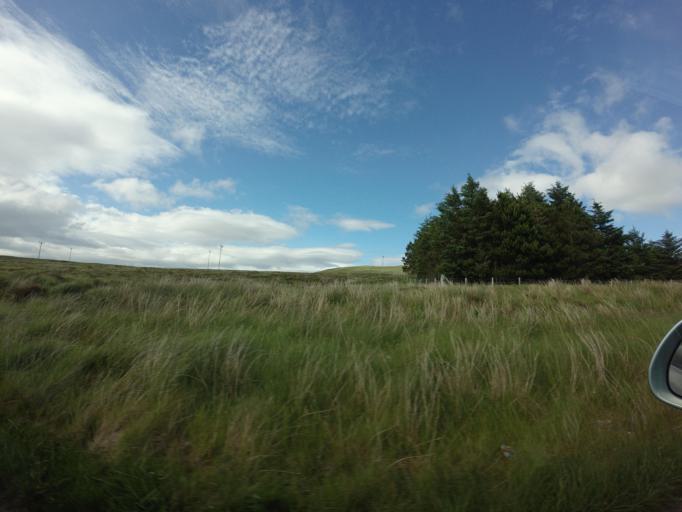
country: GB
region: Scotland
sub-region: Eilean Siar
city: Stornoway
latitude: 58.1734
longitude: -6.5976
